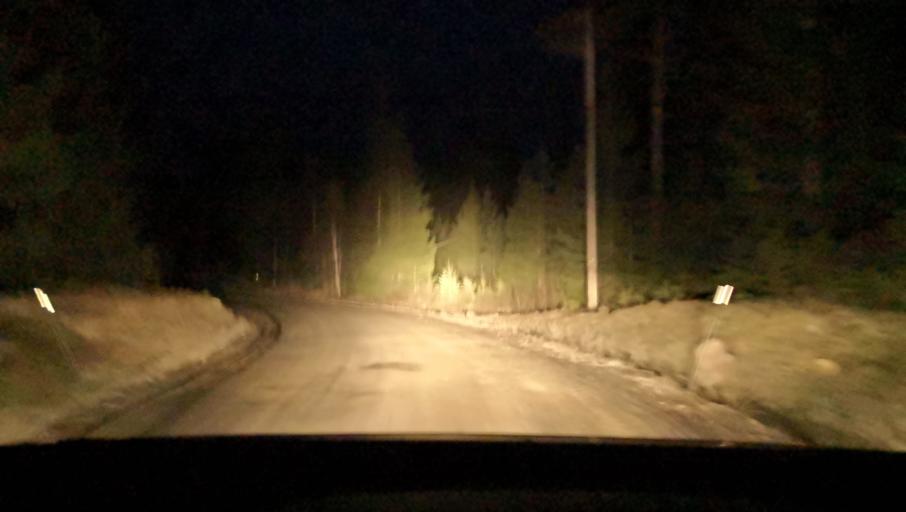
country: SE
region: Vaestmanland
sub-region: Skinnskattebergs Kommun
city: Skinnskatteberg
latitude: 59.6699
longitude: 15.5765
